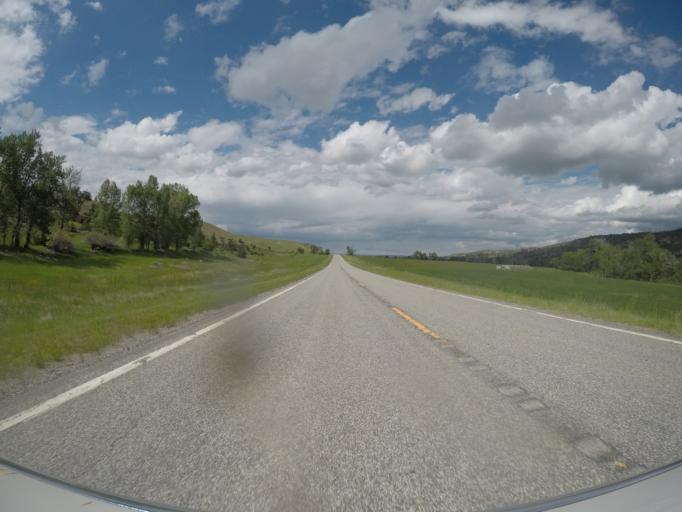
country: US
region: Montana
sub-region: Sweet Grass County
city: Big Timber
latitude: 45.7418
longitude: -109.9967
